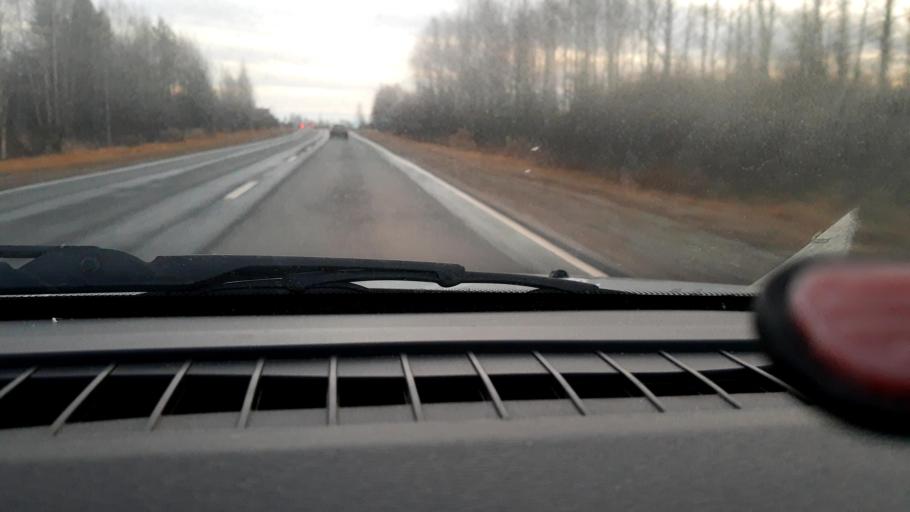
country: RU
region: Nizjnij Novgorod
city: Krasnyye Baki
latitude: 57.0911
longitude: 45.1488
